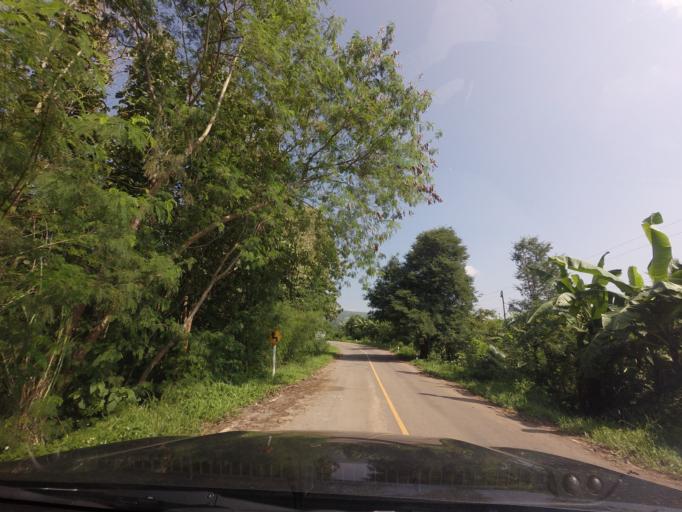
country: TH
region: Loei
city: Na Haeo
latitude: 17.4981
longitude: 101.0170
